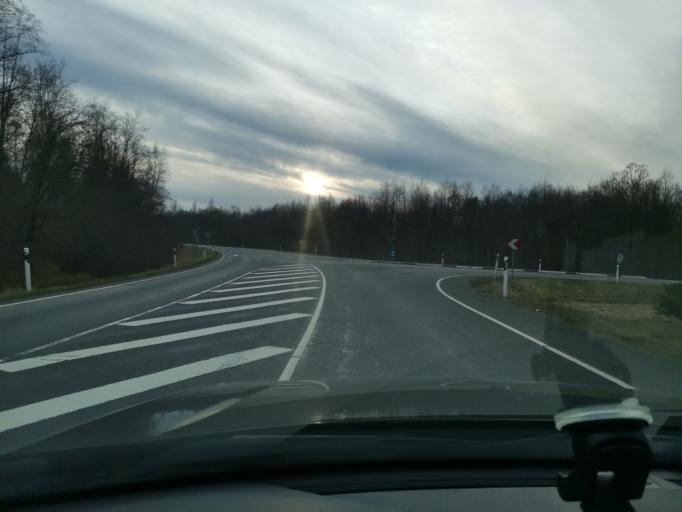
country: EE
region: Ida-Virumaa
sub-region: Sillamaee linn
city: Sillamae
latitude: 59.3237
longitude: 27.9185
